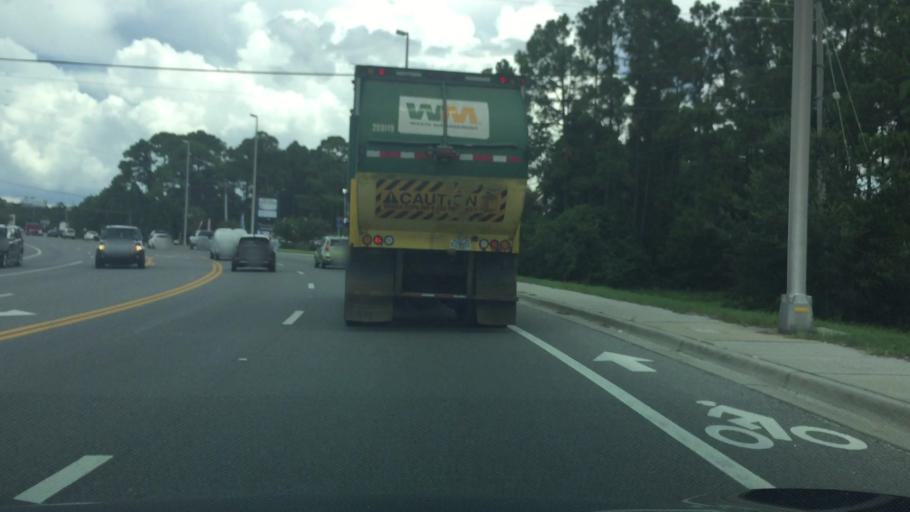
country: US
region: Florida
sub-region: Bay County
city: Lower Grand Lagoon
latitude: 30.1508
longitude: -85.7475
